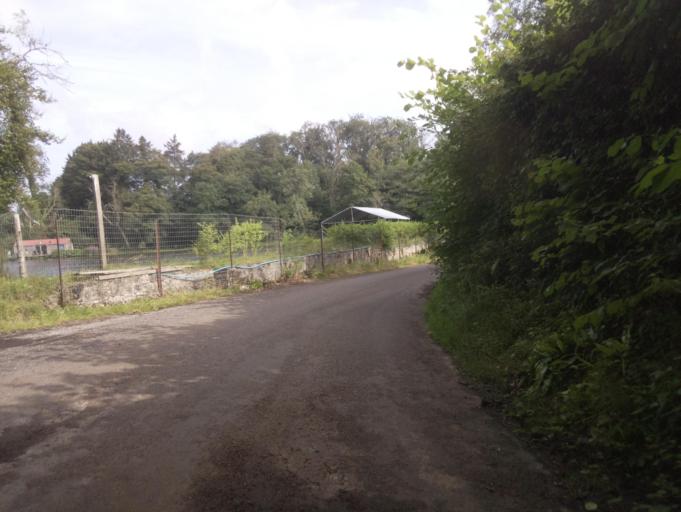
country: GB
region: England
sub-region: Somerset
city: Chilcompton
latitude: 51.2562
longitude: -2.5523
